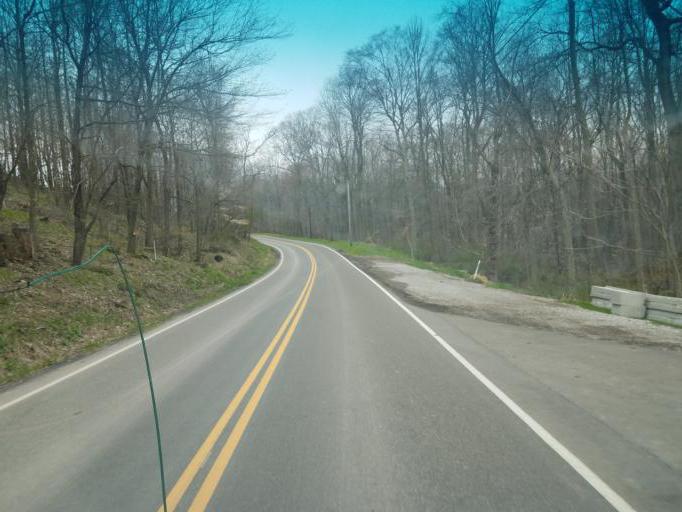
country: US
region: Ohio
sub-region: Stark County
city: Beach City
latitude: 40.6123
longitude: -81.6774
